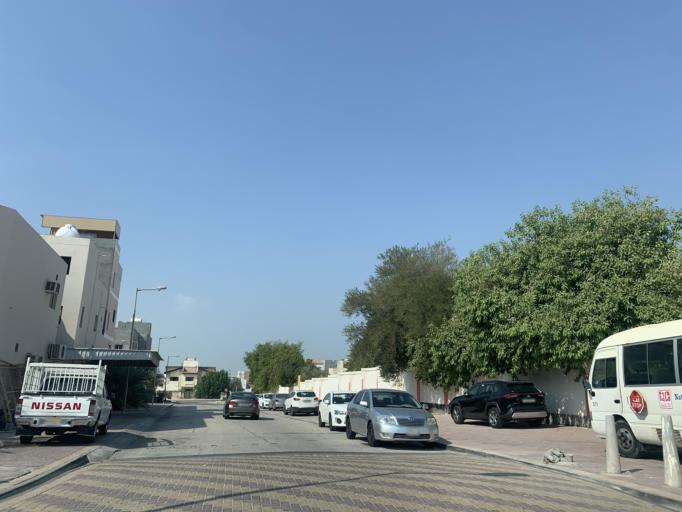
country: BH
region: Central Governorate
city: Madinat Hamad
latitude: 26.1118
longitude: 50.4998
